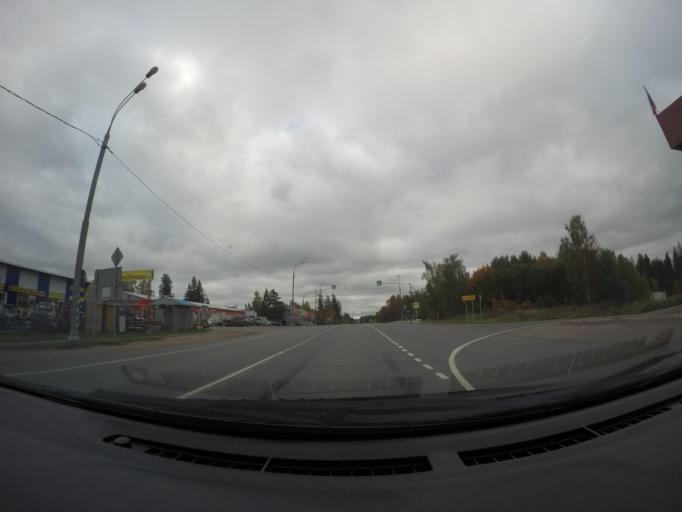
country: RU
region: Moskovskaya
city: Dorokhovo
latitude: 55.6224
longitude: 36.3429
